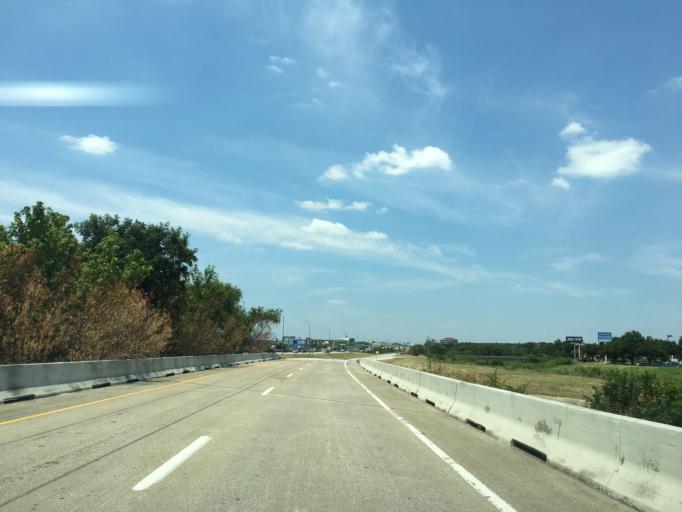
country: US
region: Texas
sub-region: Denton County
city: Lewisville
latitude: 33.0103
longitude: -96.9762
